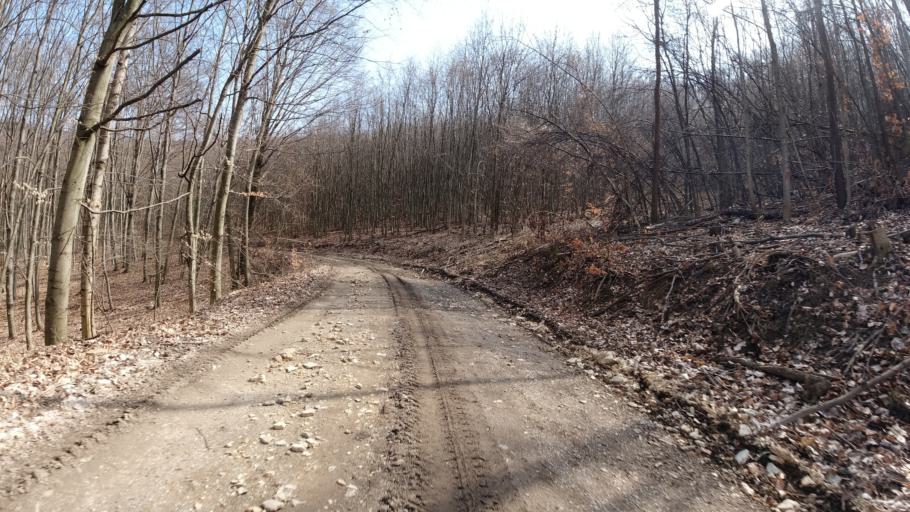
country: SK
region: Trnavsky
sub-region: Okres Trnava
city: Piestany
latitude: 48.5996
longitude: 17.9468
